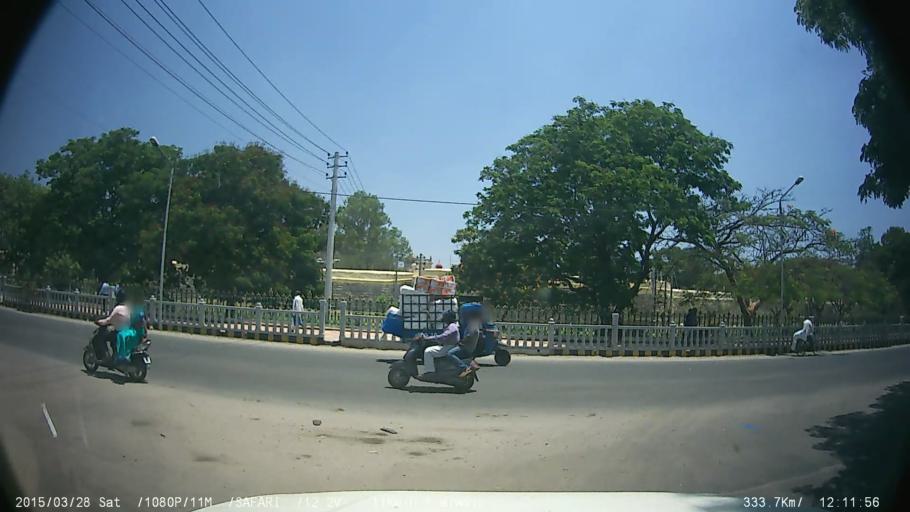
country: IN
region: Karnataka
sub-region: Mysore
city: Mysore
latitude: 12.3052
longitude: 76.6517
